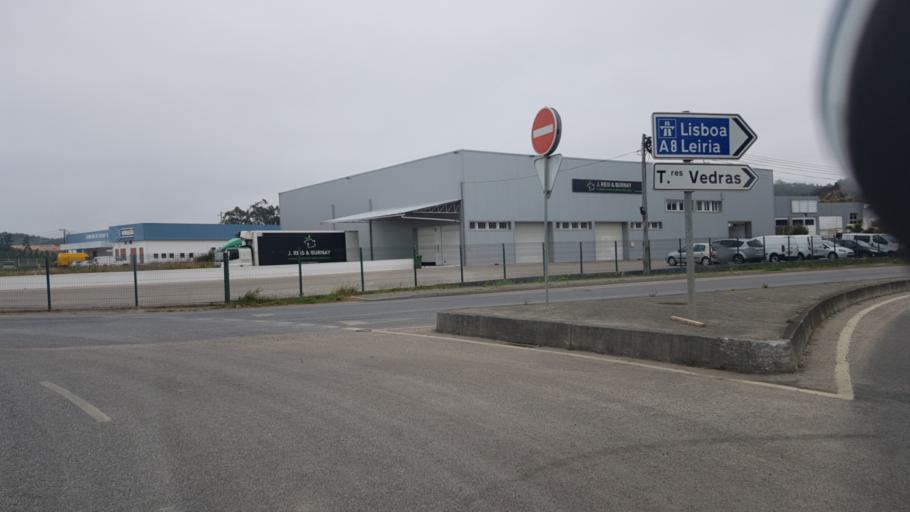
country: PT
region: Lisbon
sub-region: Torres Vedras
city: Torres Vedras
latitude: 39.0973
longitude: -9.2806
